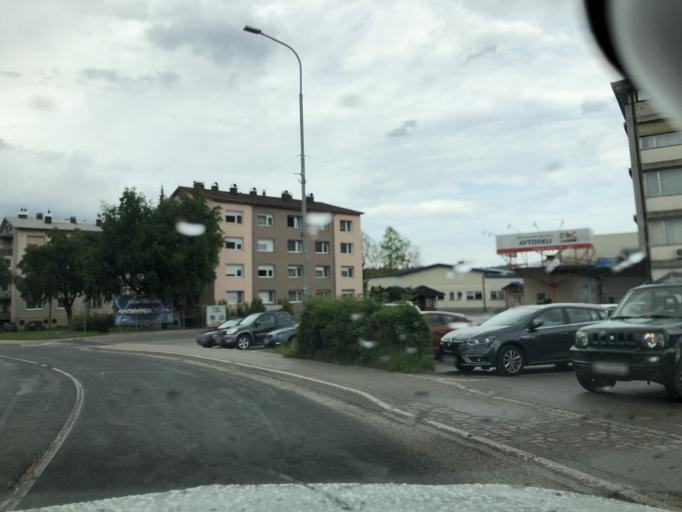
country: SI
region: Cerknica
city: Cerknica
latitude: 45.7928
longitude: 14.3663
